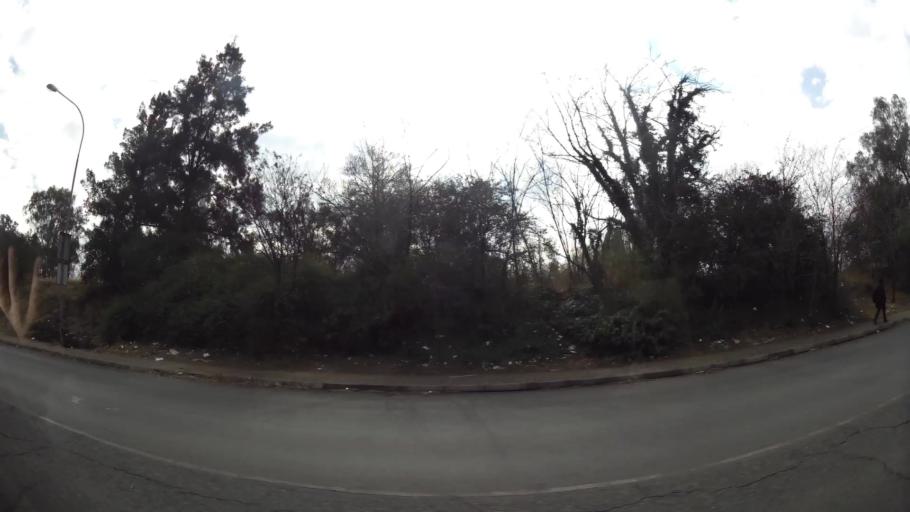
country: ZA
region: Gauteng
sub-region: Sedibeng District Municipality
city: Vereeniging
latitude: -26.6815
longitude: 27.9358
